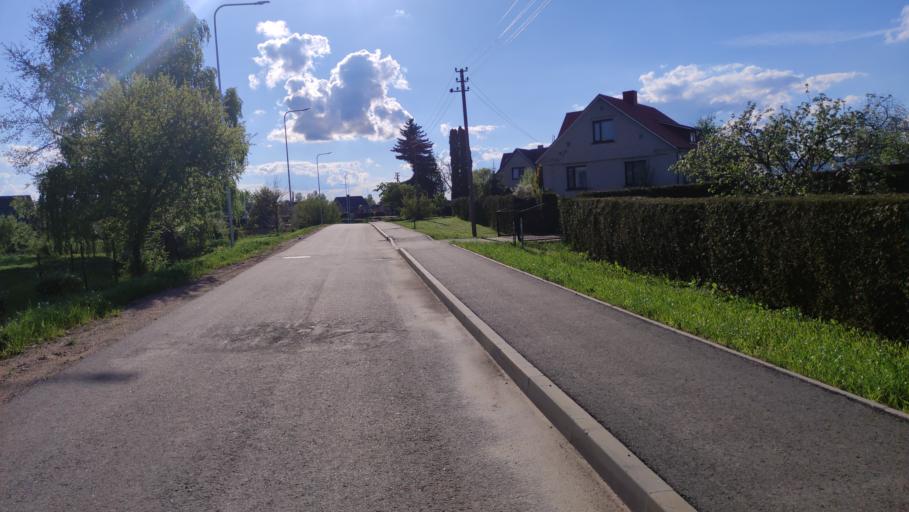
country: LT
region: Alytaus apskritis
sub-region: Alytus
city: Alytus
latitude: 54.4367
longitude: 23.9989
